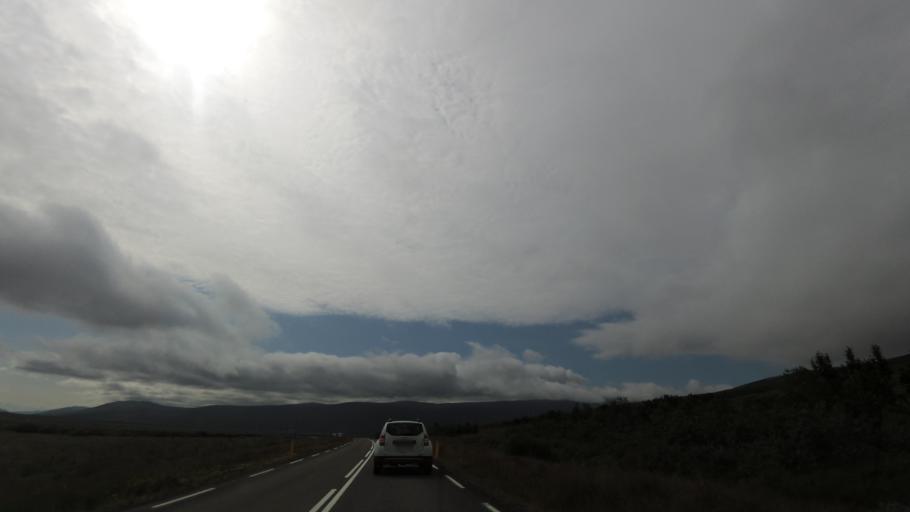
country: IS
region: Northeast
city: Laugar
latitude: 65.7251
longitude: -17.5961
